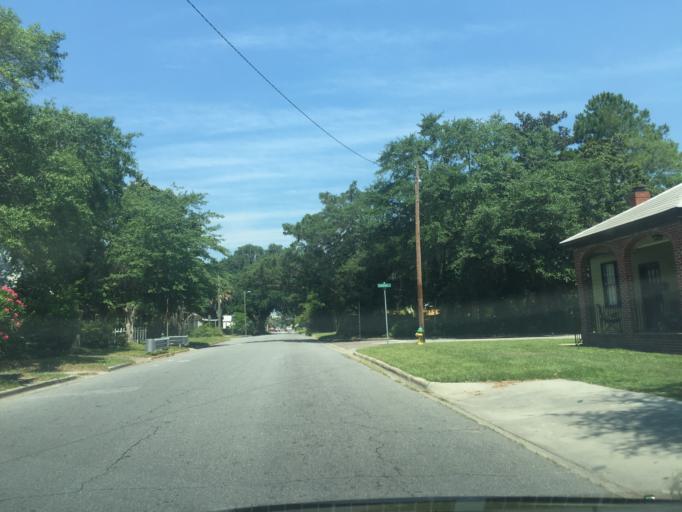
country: US
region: Georgia
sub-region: Chatham County
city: Savannah
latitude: 32.0462
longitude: -81.1059
